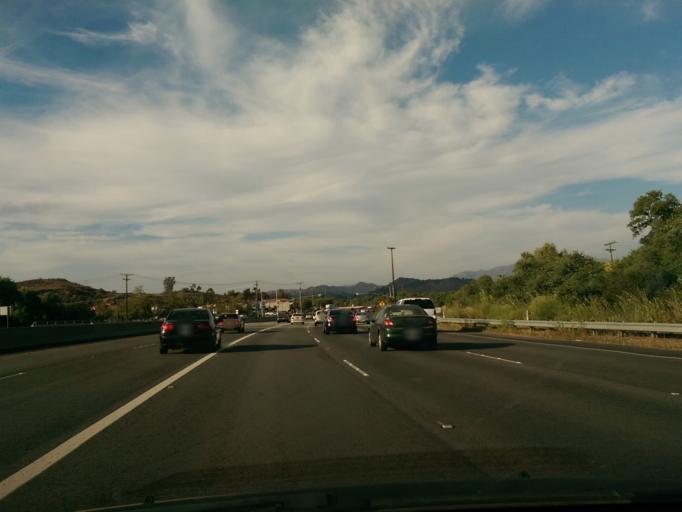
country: US
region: California
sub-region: San Diego County
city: Bonsall
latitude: 33.2924
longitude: -117.2240
